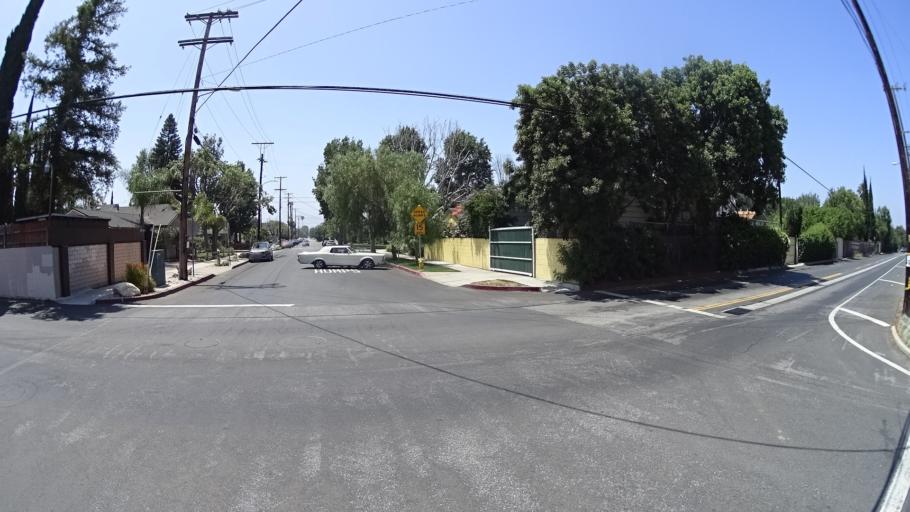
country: US
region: California
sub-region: Los Angeles County
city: Van Nuys
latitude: 34.2072
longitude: -118.4444
